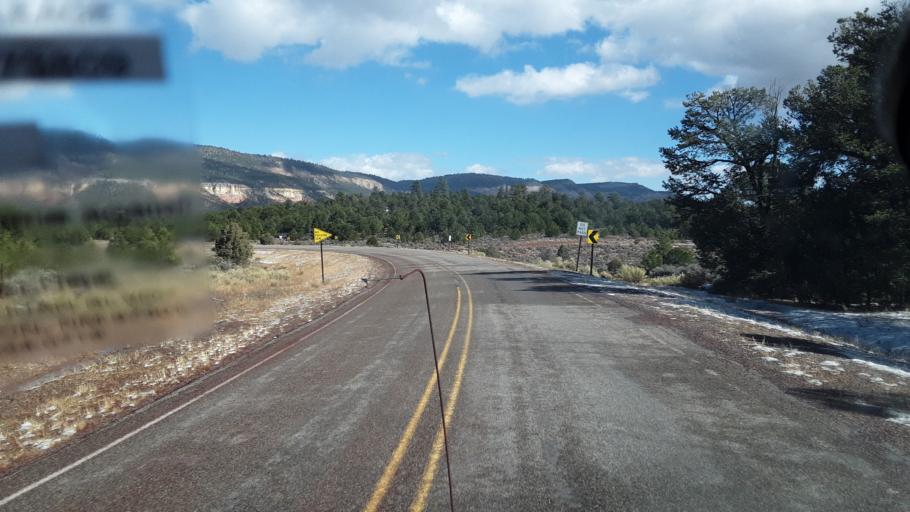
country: US
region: New Mexico
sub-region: Rio Arriba County
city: Santa Teresa
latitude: 36.1949
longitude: -106.7405
